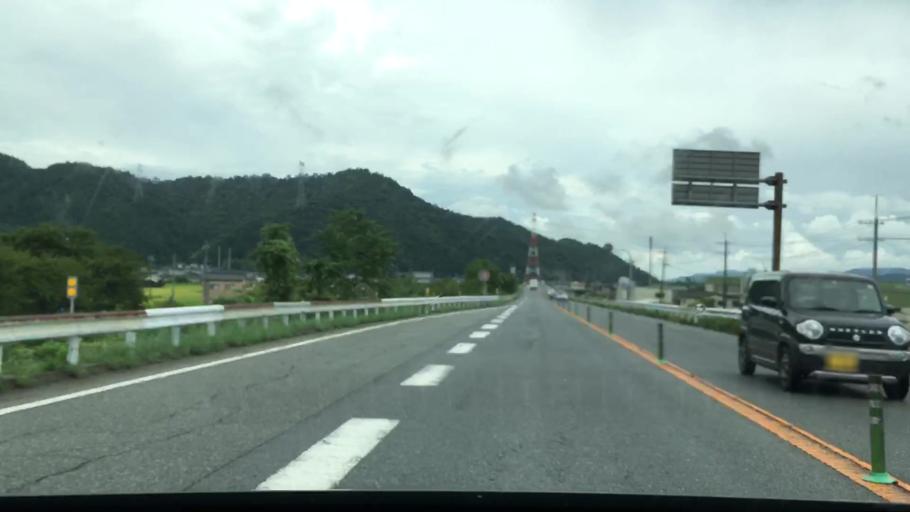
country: JP
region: Hyogo
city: Himeji
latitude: 34.9815
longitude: 134.7693
